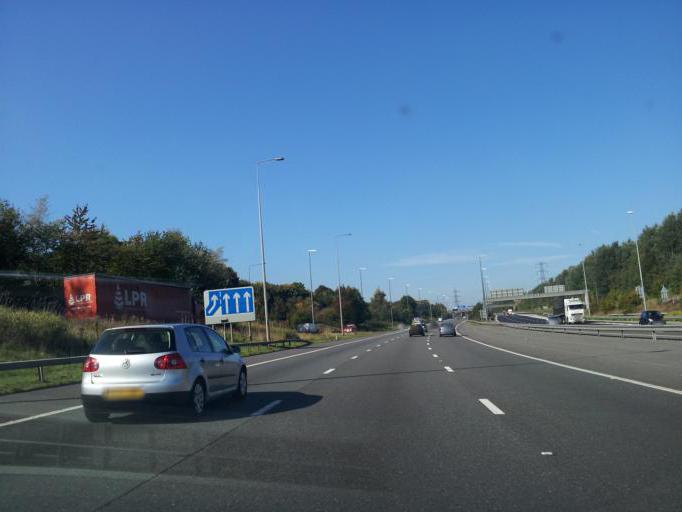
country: GB
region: England
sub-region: Manchester
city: Crumpsall
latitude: 53.5402
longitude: -2.2388
